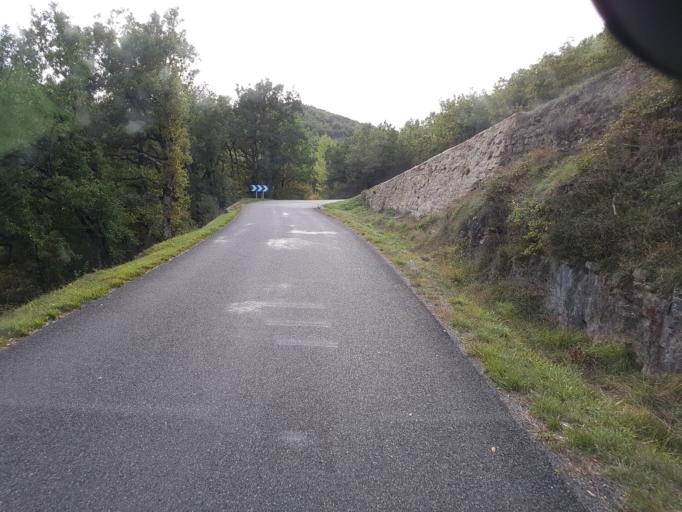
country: FR
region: Midi-Pyrenees
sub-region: Departement de l'Aveyron
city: Saint-Affrique
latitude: 43.9975
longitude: 2.9496
